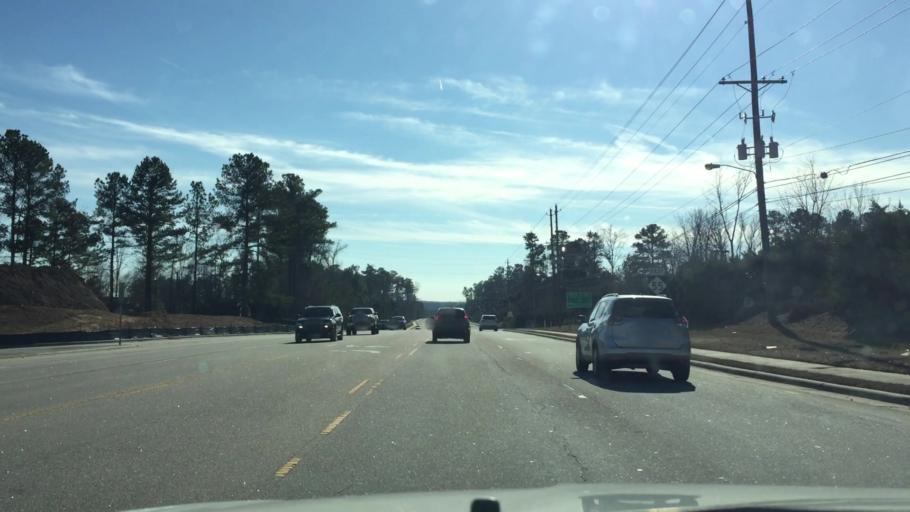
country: US
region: North Carolina
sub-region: Wake County
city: Green Level
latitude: 35.7602
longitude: -78.8758
